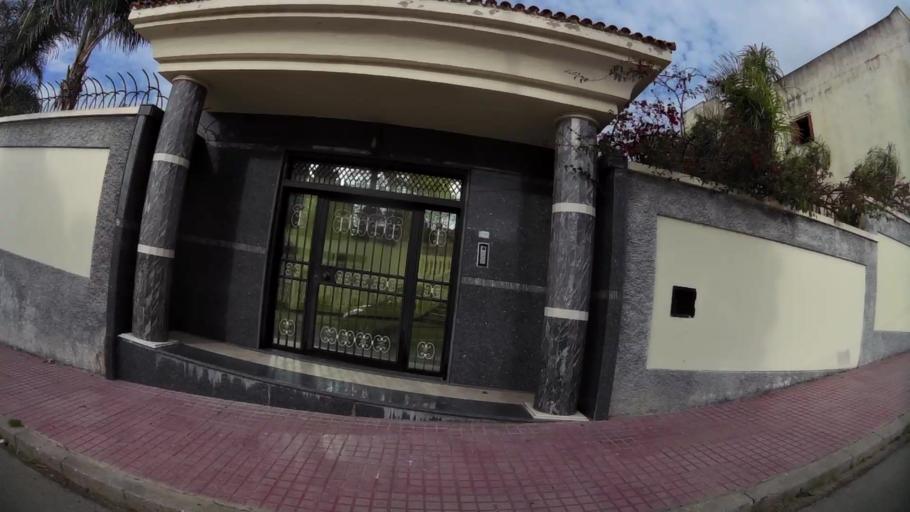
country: MA
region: Tanger-Tetouan
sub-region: Tanger-Assilah
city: Tangier
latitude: 35.7688
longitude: -5.7924
